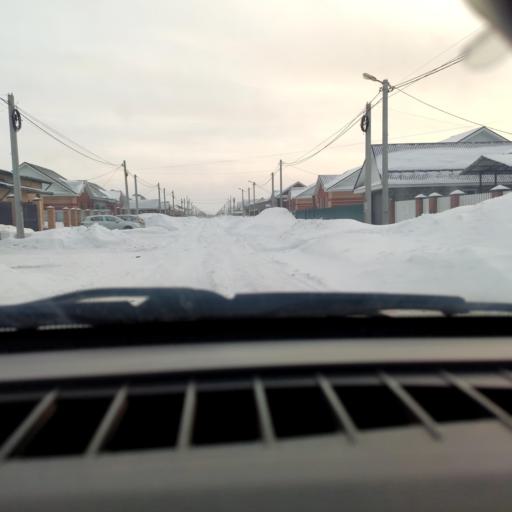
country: RU
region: Bashkortostan
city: Kabakovo
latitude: 54.6123
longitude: 56.1204
